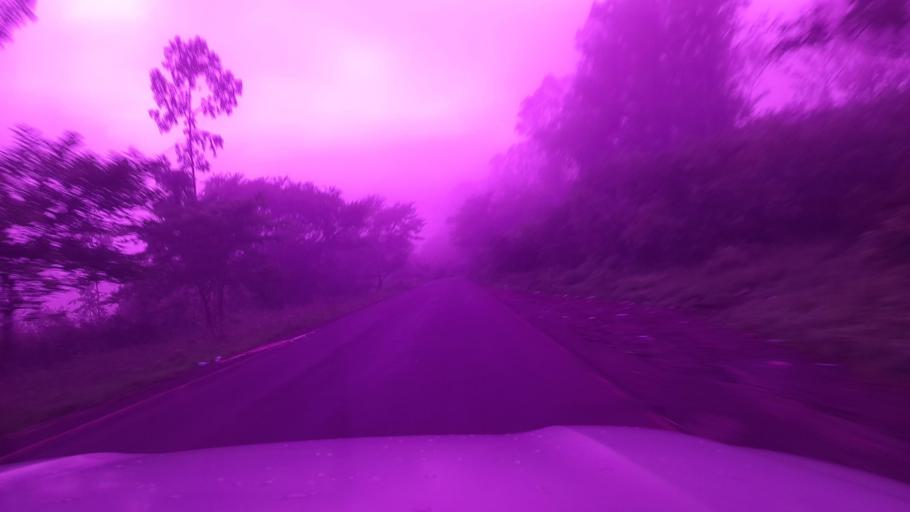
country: ET
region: Oromiya
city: Waliso
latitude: 8.1695
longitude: 37.5485
